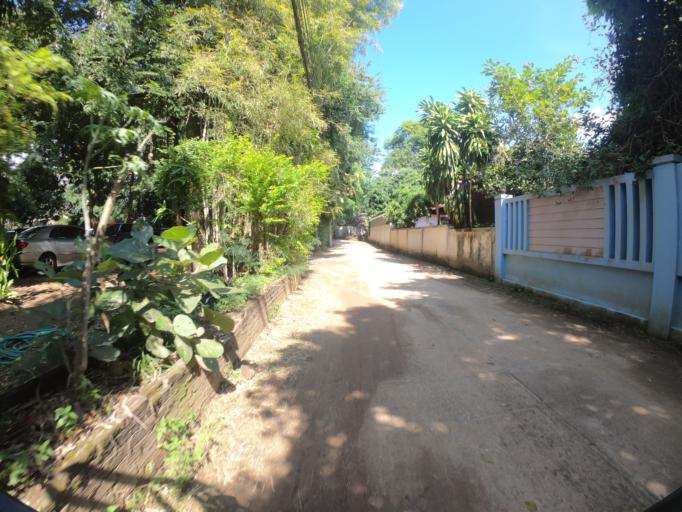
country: TH
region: Chiang Mai
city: Chiang Mai
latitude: 18.7753
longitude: 98.9494
